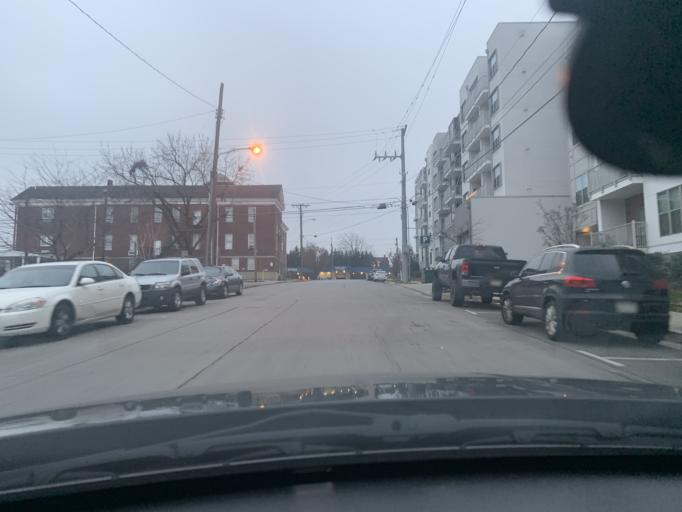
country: US
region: Tennessee
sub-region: Davidson County
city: Nashville
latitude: 36.1748
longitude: -86.7634
